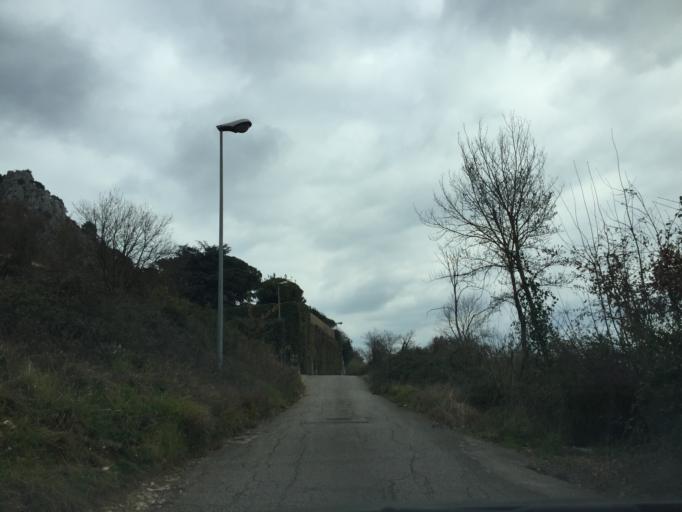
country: IT
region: Latium
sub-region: Provincia di Frosinone
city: Cassino
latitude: 41.4815
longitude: 13.8071
